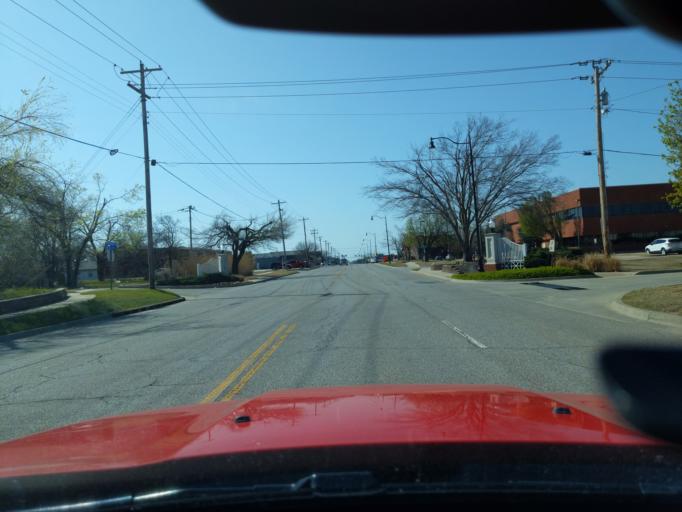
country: US
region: Oklahoma
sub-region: Cleveland County
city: Moore
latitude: 35.3418
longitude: -97.4867
